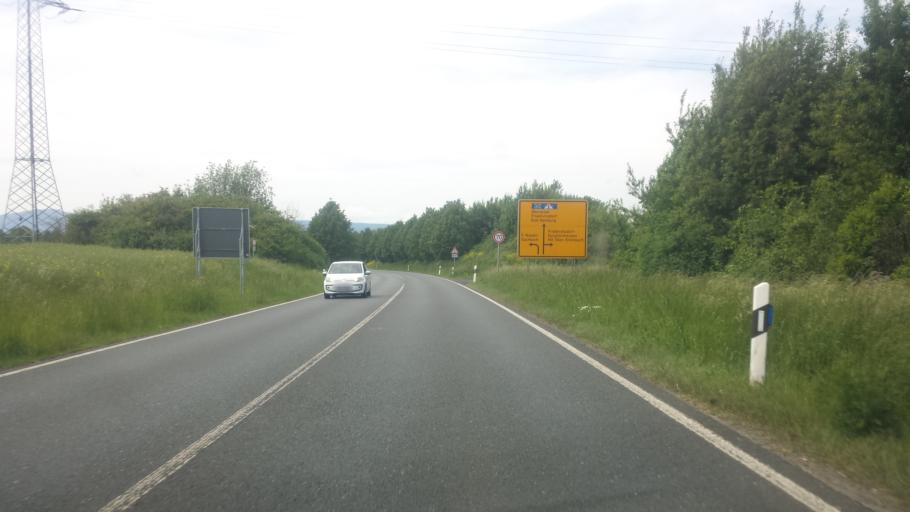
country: DE
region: Hesse
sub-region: Regierungsbezirk Darmstadt
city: Friedrichsdorf
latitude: 50.2186
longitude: 8.6862
